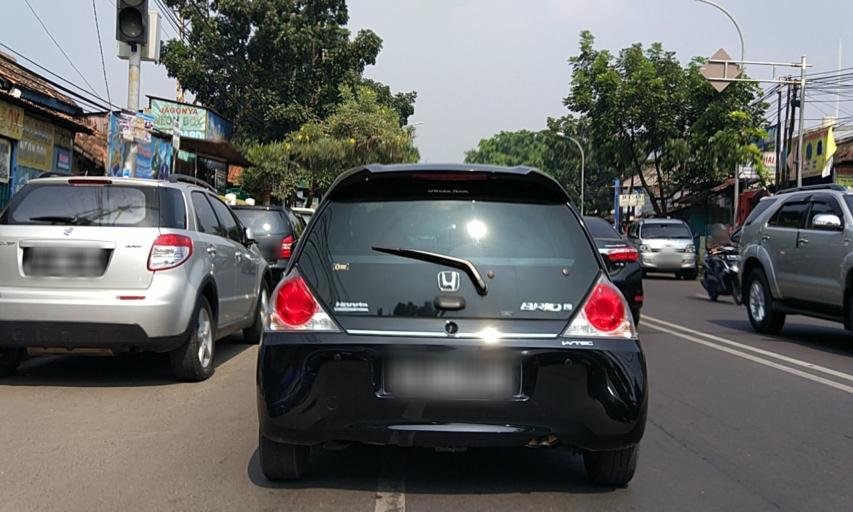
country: ID
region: West Java
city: Bandung
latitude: -6.8991
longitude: 107.6310
